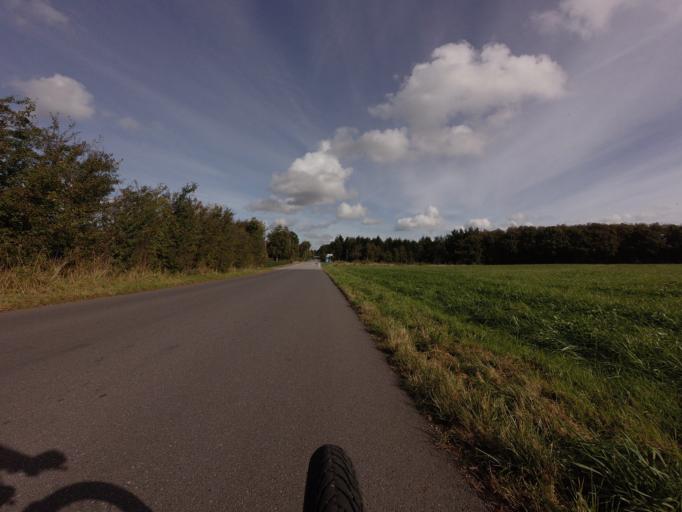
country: DK
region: Central Jutland
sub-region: Viborg Kommune
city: Bjerringbro
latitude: 56.4762
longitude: 9.6198
